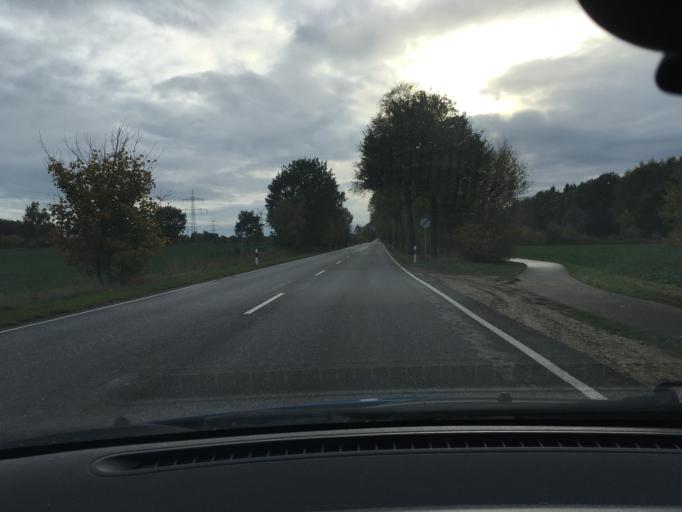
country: DE
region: Schleswig-Holstein
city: Talkau
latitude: 53.5590
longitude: 10.5555
